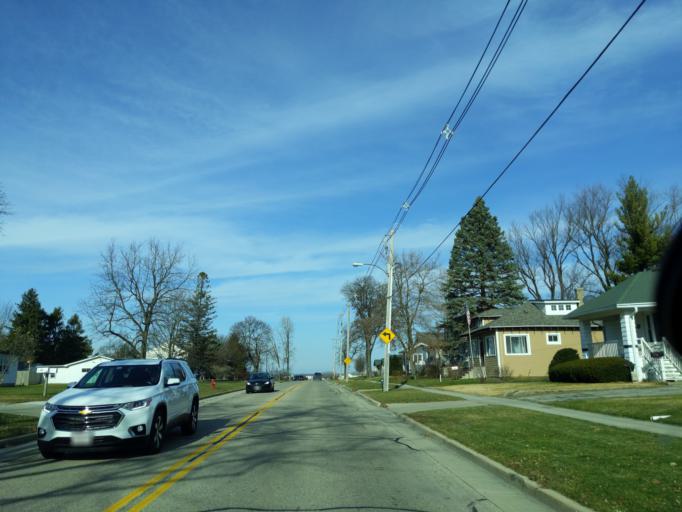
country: US
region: Wisconsin
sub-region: Walworth County
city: Elkhorn
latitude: 42.6828
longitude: -88.5464
